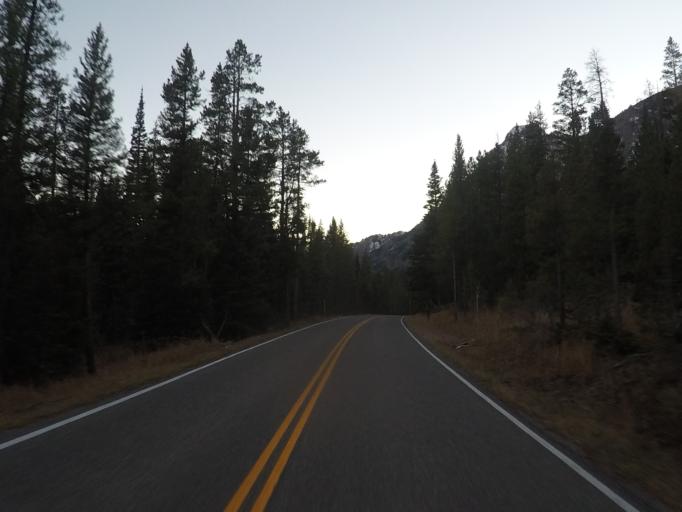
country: US
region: Montana
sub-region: Stillwater County
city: Absarokee
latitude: 44.9955
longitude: -110.0541
